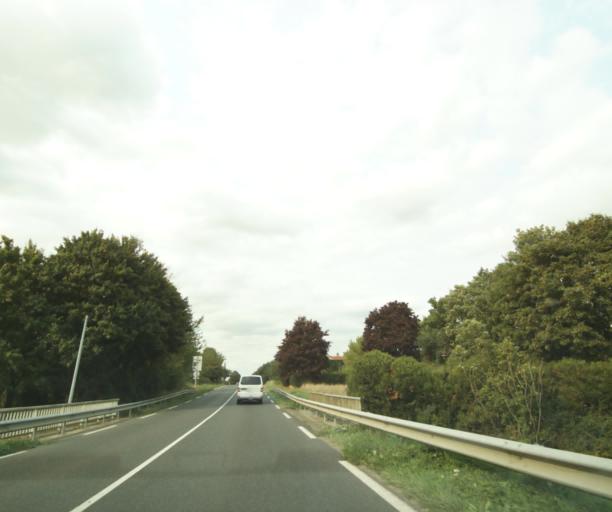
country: FR
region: Centre
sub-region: Departement de l'Indre
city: Chatillon-sur-Indre
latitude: 47.0367
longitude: 1.0956
